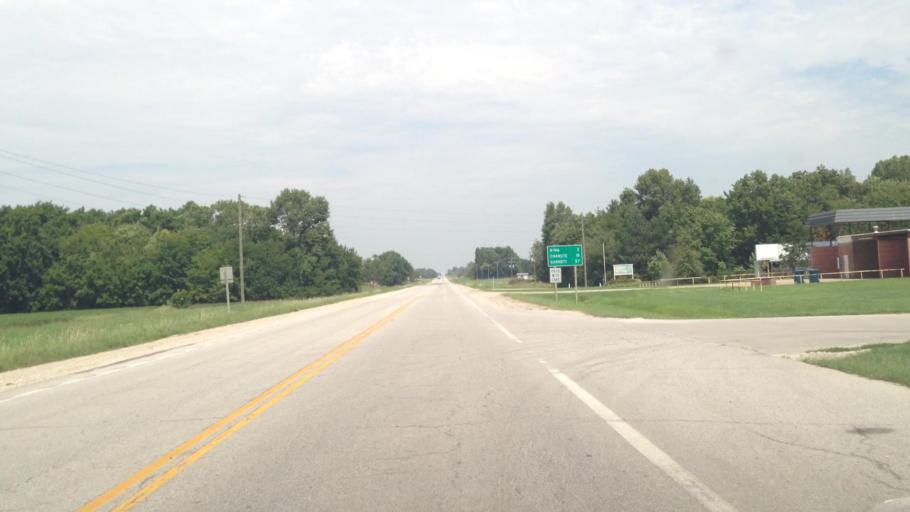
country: US
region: Kansas
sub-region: Neosho County
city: Erie
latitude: 37.5739
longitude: -95.2525
